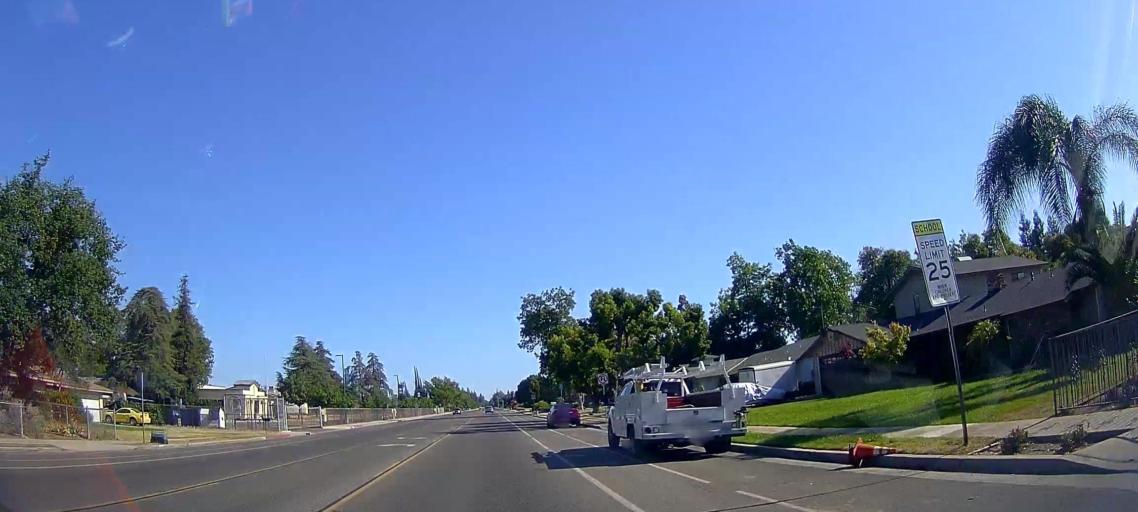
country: US
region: California
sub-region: Fresno County
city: Fresno
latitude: 36.8189
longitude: -119.7994
